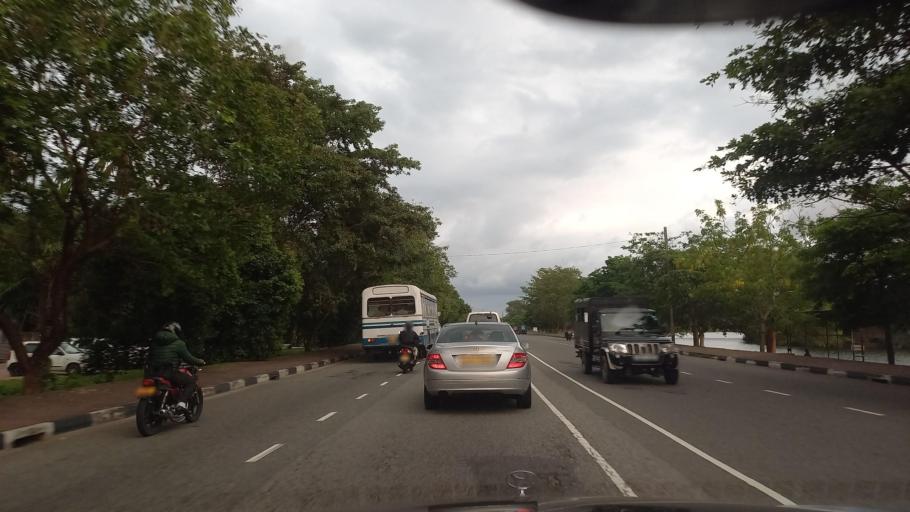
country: LK
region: Western
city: Battaramulla South
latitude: 6.8849
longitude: 79.9248
